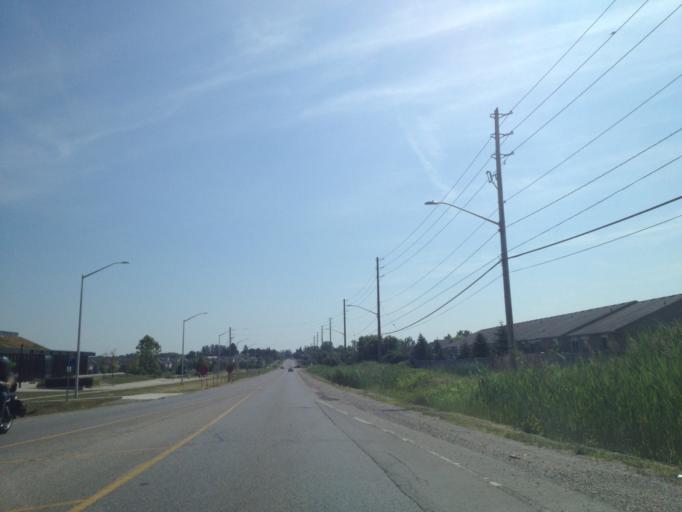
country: CA
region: Ontario
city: London
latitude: 43.0472
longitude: -81.2588
